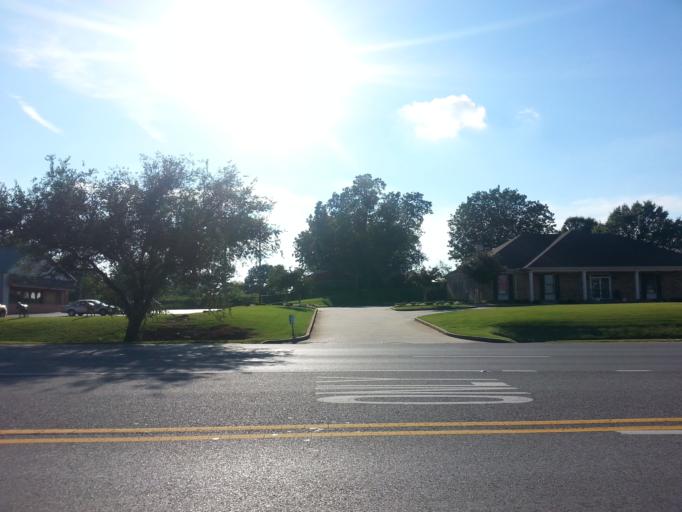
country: US
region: Alabama
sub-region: Colbert County
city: Muscle Shoals
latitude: 34.7295
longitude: -87.6678
